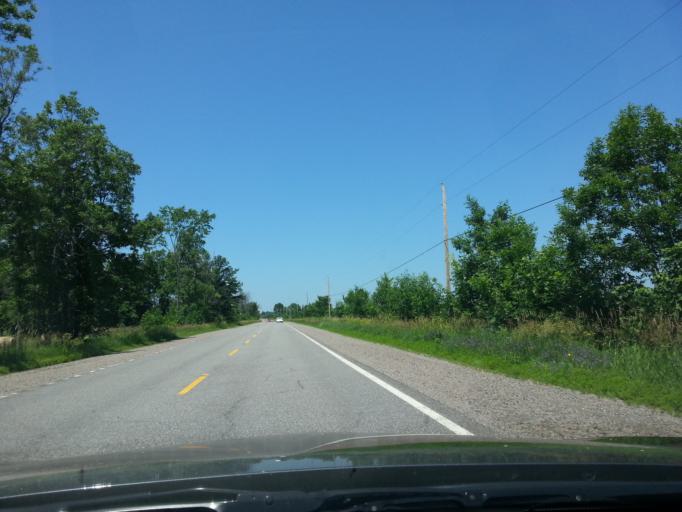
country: CA
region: Ontario
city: Arnprior
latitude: 45.5388
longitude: -76.3278
